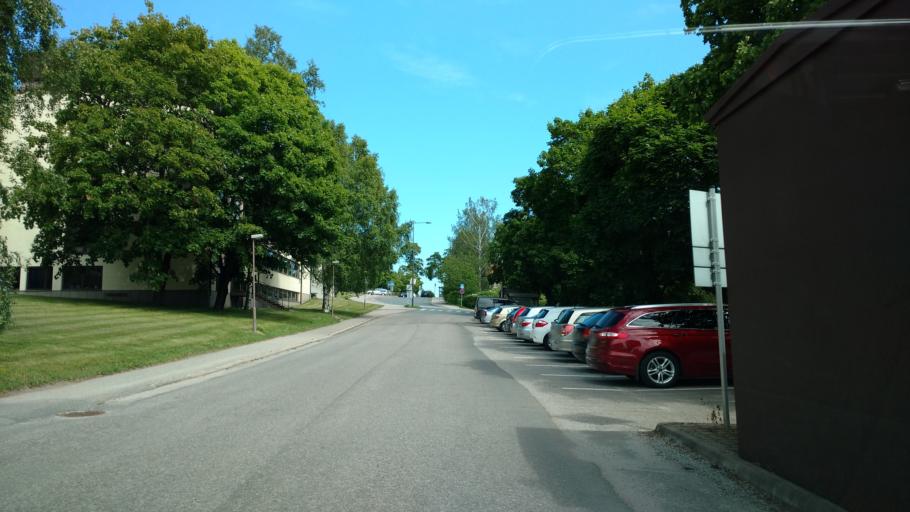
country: FI
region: Varsinais-Suomi
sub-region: Salo
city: Salo
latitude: 60.3747
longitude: 23.1278
